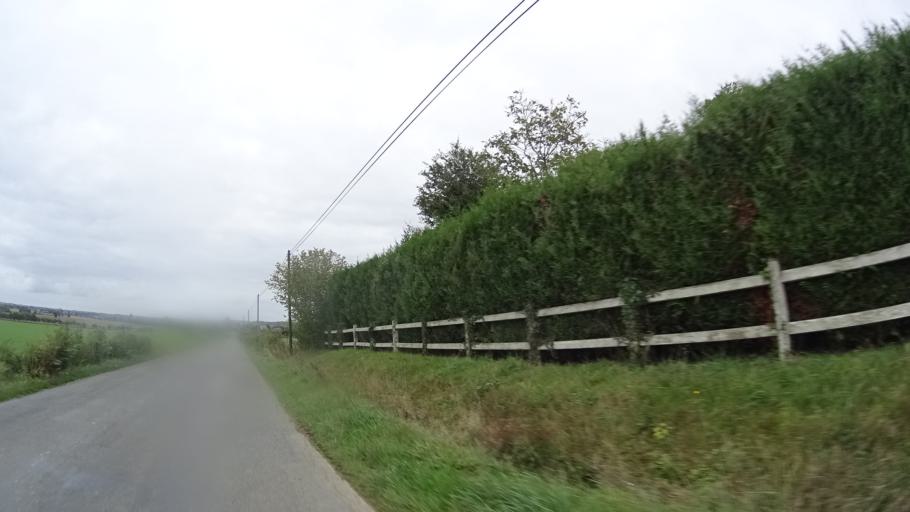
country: FR
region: Brittany
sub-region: Departement d'Ille-et-Vilaine
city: Paimpont
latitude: 48.0936
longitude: -2.1218
